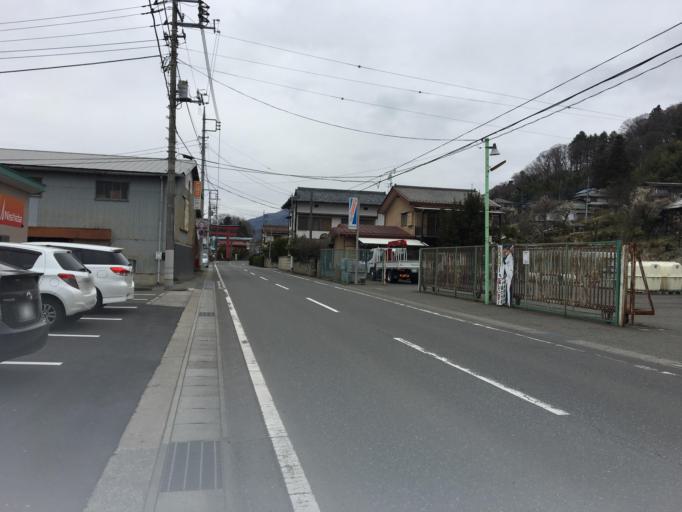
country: JP
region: Gunma
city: Numata
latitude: 36.6456
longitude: 139.0368
